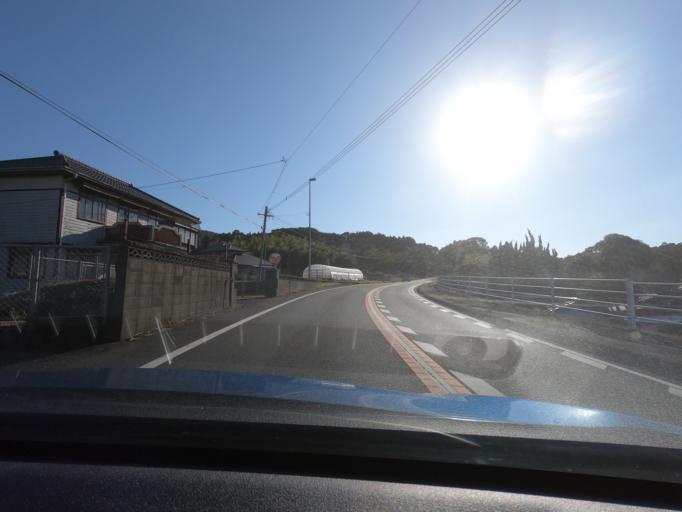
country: JP
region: Kumamoto
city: Minamata
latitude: 32.1712
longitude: 130.3810
